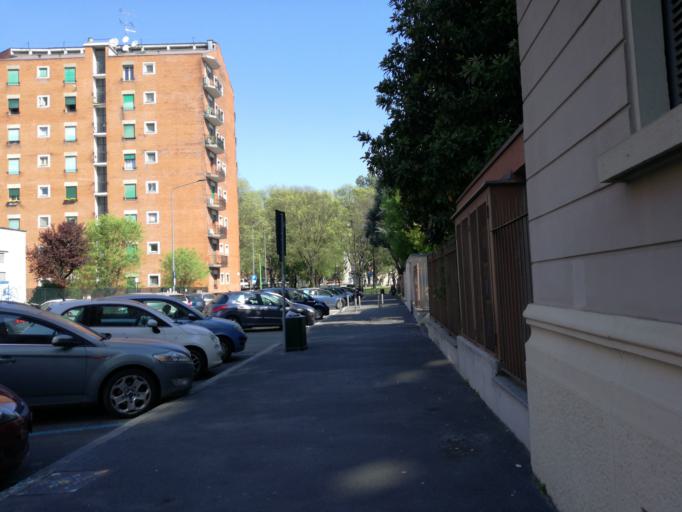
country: IT
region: Lombardy
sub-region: Citta metropolitana di Milano
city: Milano
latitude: 45.4319
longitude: 9.1840
